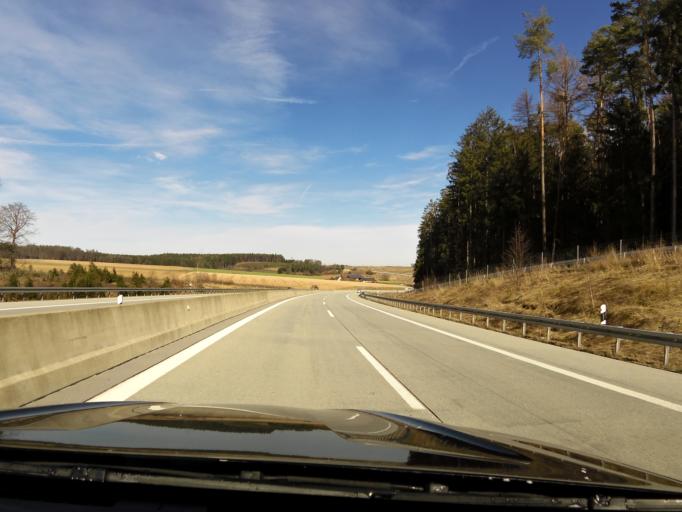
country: DE
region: Bavaria
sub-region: Upper Palatinate
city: Schierling
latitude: 48.7688
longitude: 12.1340
